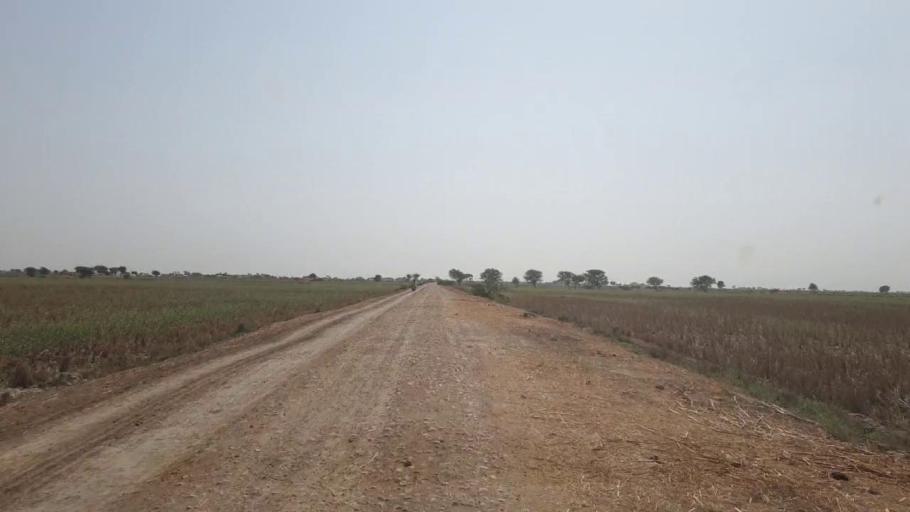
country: PK
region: Sindh
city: Jati
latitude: 24.4360
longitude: 68.5523
